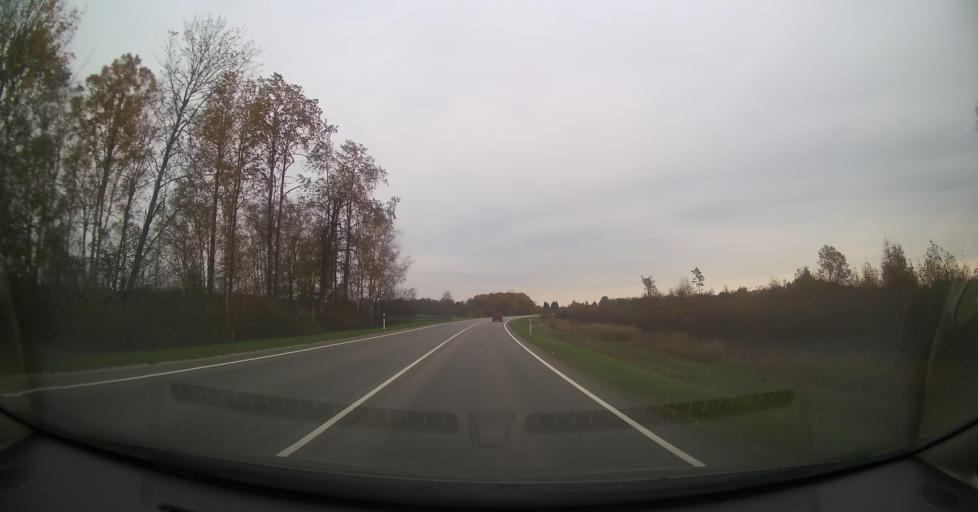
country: EE
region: Laeaene
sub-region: Ridala Parish
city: Uuemoisa
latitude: 58.9739
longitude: 23.8490
